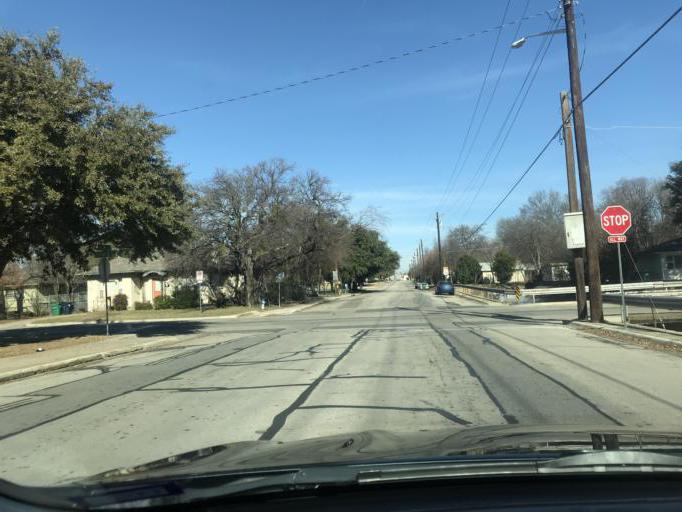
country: US
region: Texas
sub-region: Denton County
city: Denton
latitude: 33.2253
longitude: -97.1433
